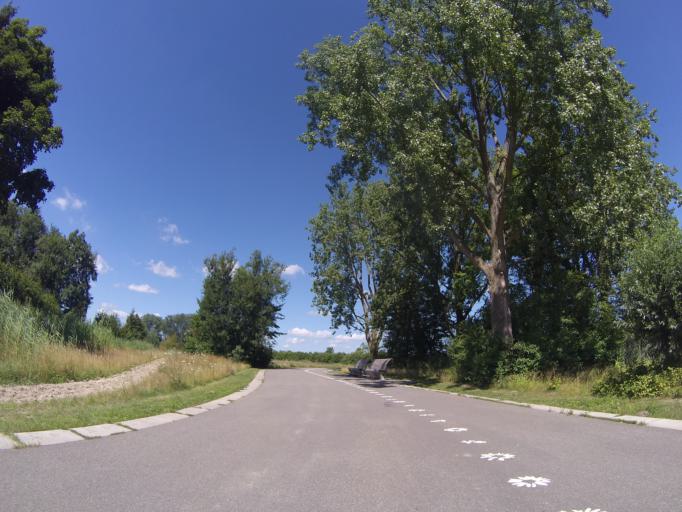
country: NL
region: Utrecht
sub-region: Stichtse Vecht
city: Maarssen
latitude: 52.1040
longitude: 5.0302
